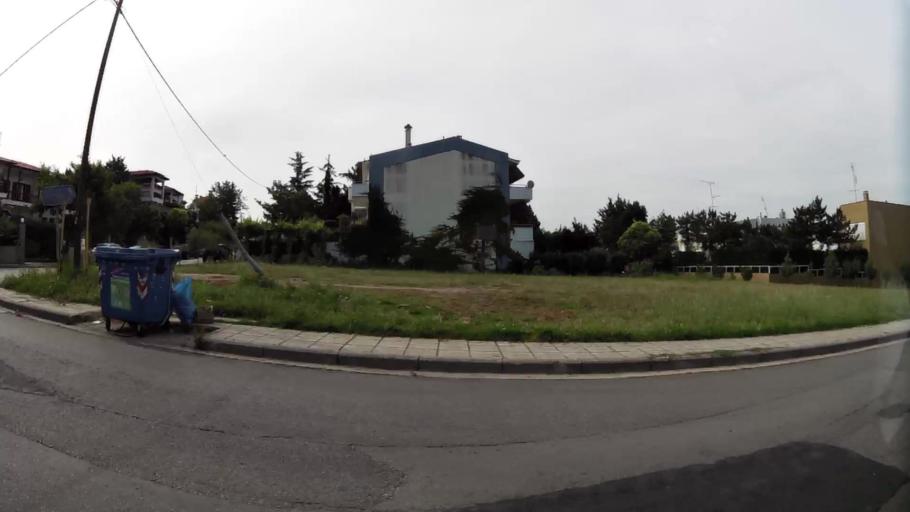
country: GR
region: Central Macedonia
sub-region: Nomos Thessalonikis
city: Panorama
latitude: 40.5778
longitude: 23.0193
